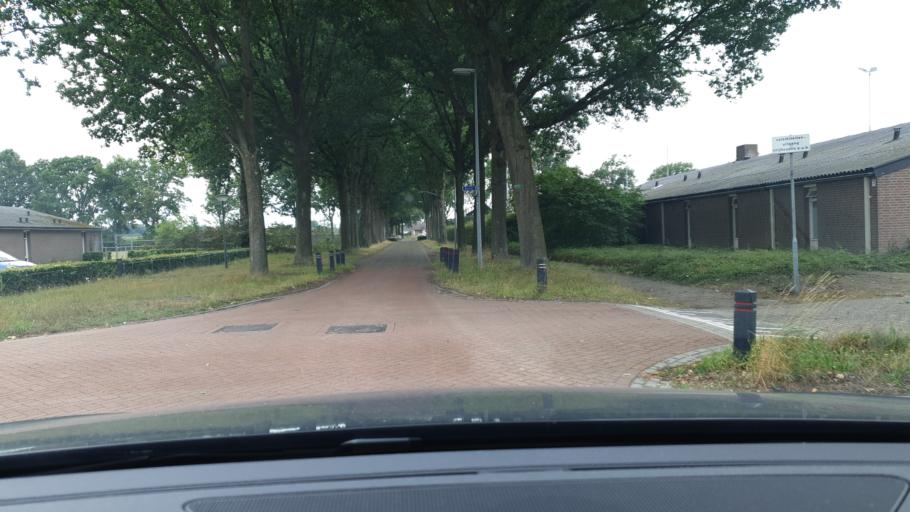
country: NL
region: North Brabant
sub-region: Gemeente Veldhoven
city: Oerle
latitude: 51.4297
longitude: 5.3787
